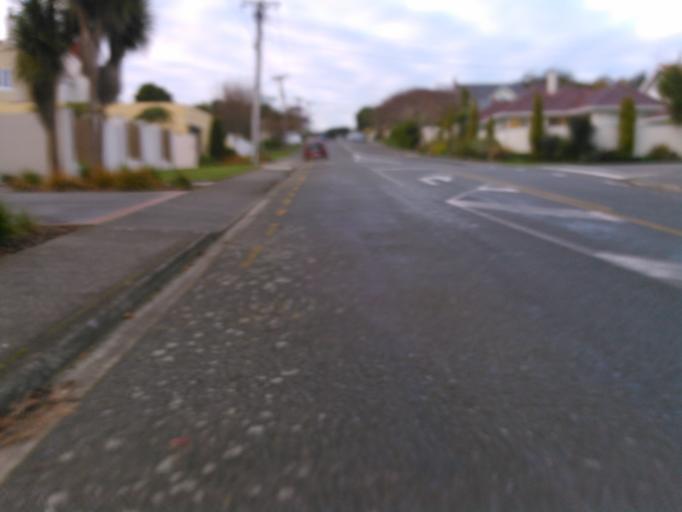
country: NZ
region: Wellington
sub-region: Wellington City
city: Kelburn
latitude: -41.2821
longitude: 174.7391
